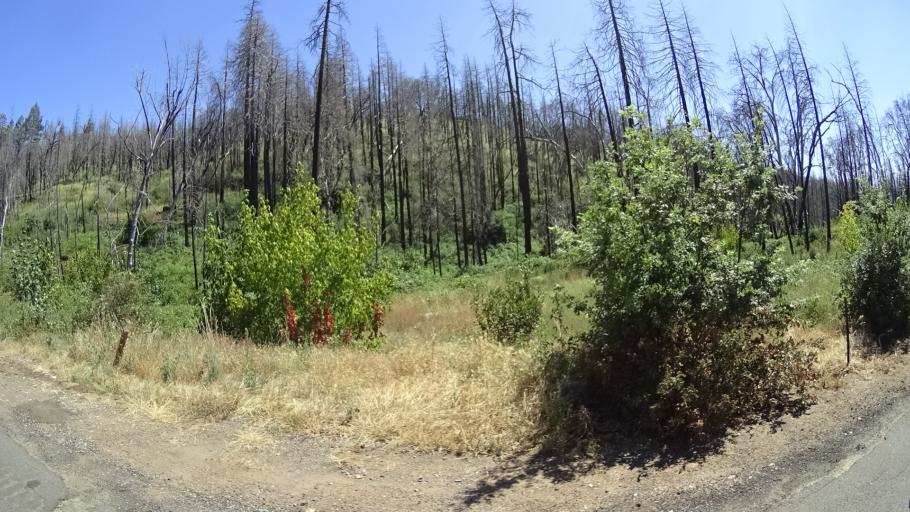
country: US
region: California
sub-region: Calaveras County
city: Mountain Ranch
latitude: 38.2833
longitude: -120.5703
